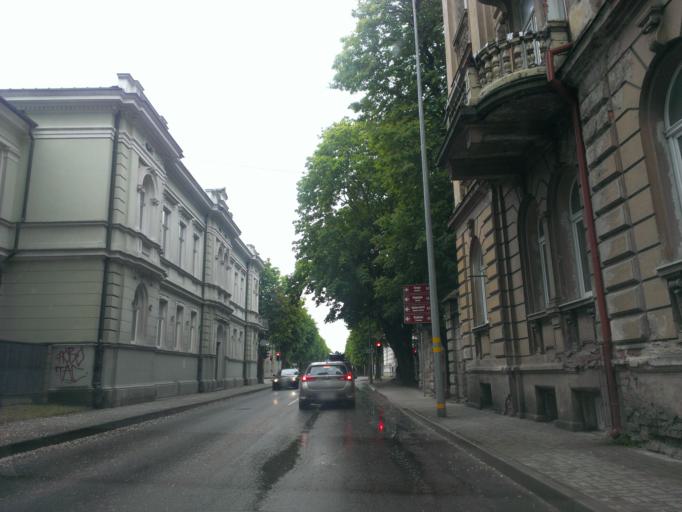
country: LV
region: Liepaja
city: Liepaja
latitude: 56.5053
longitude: 21.0016
